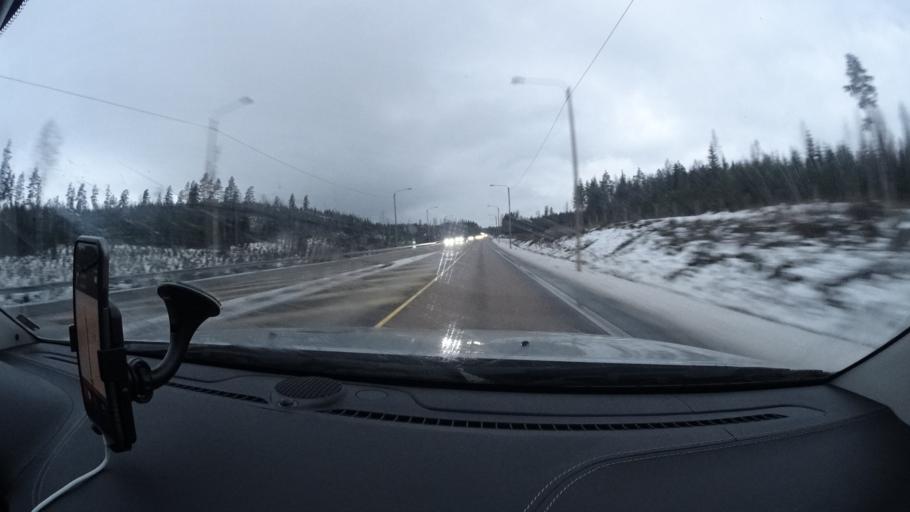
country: FI
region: Central Finland
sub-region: Joutsa
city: Leivonmaeki
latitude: 61.9887
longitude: 26.0598
